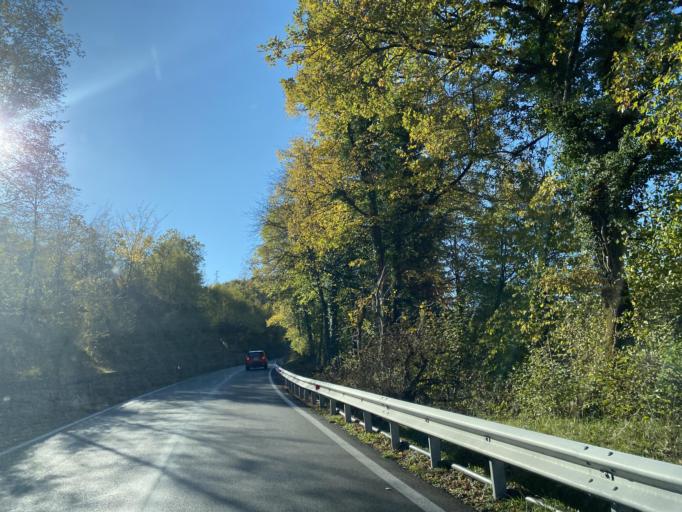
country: IT
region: Lombardy
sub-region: Provincia di Como
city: Osteno-Claino
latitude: 45.9961
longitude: 9.0824
